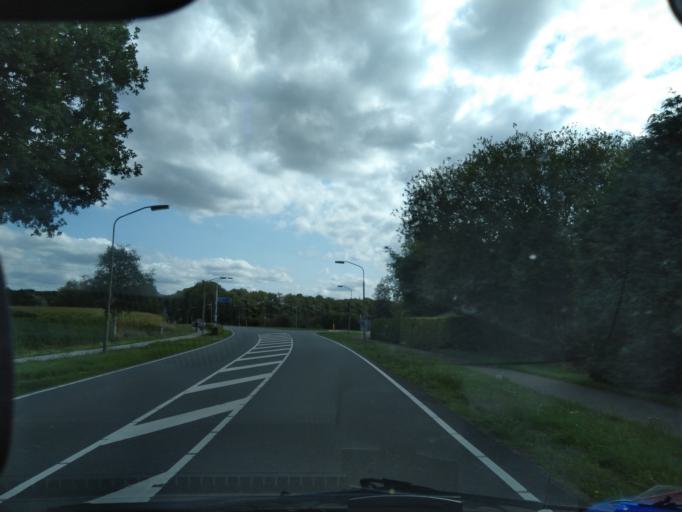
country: NL
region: Groningen
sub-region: Gemeente Haren
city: Haren
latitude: 53.1351
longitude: 6.5796
